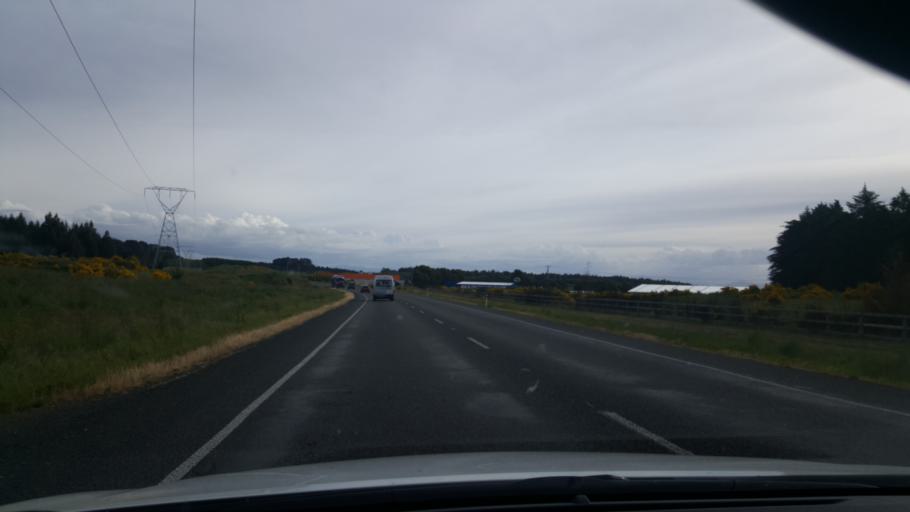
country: NZ
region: Waikato
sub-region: Taupo District
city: Taupo
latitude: -38.6977
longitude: 176.1127
